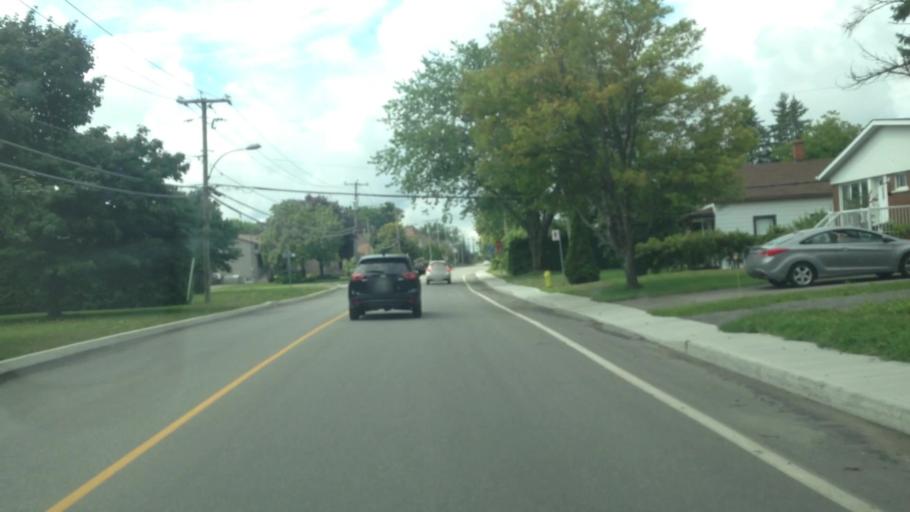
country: CA
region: Quebec
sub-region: Laurentides
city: Blainville
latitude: 45.7013
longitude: -73.9321
